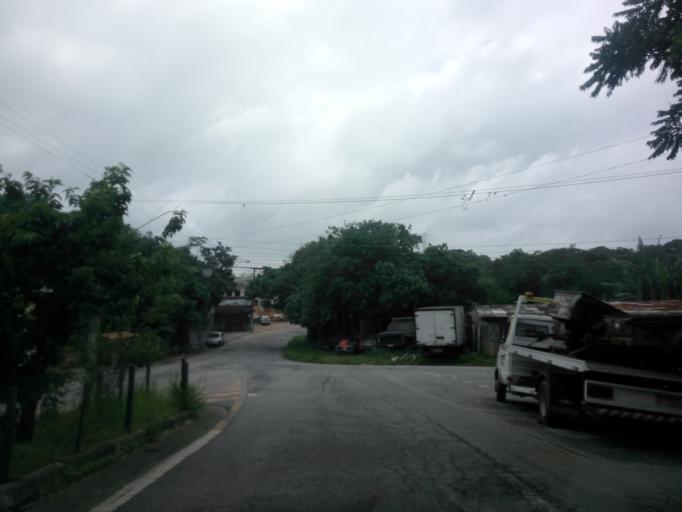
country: BR
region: Sao Paulo
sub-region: Sao Bernardo Do Campo
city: Sao Bernardo do Campo
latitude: -23.7997
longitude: -46.5422
